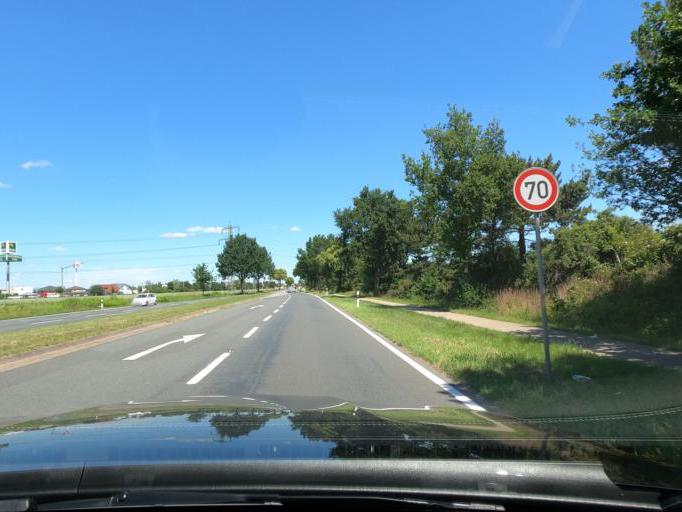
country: DE
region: Lower Saxony
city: Lehrte
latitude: 52.3908
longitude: 9.9719
